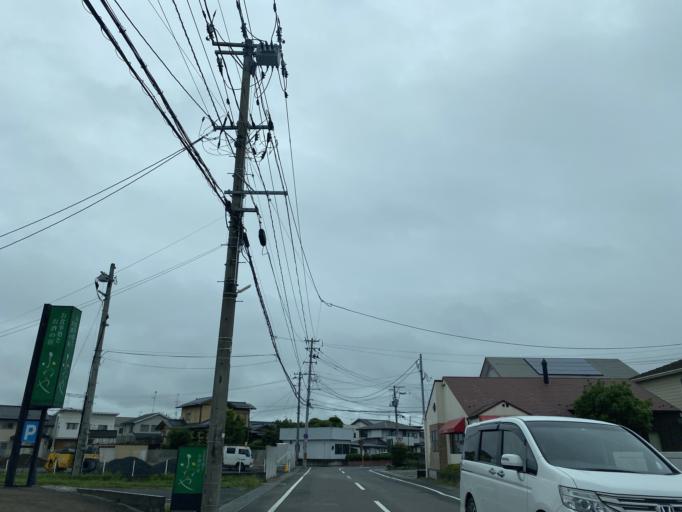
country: JP
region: Fukushima
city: Koriyama
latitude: 37.3959
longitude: 140.3306
